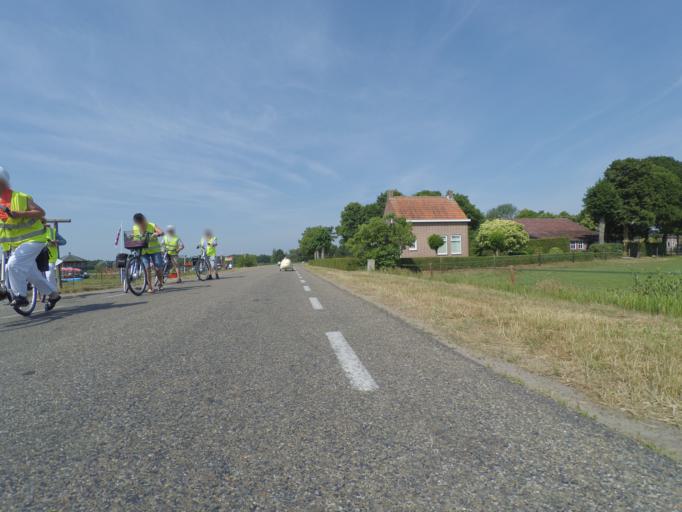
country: NL
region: North Brabant
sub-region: Gemeente Zundert
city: Zundert
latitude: 51.5124
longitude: 4.6665
